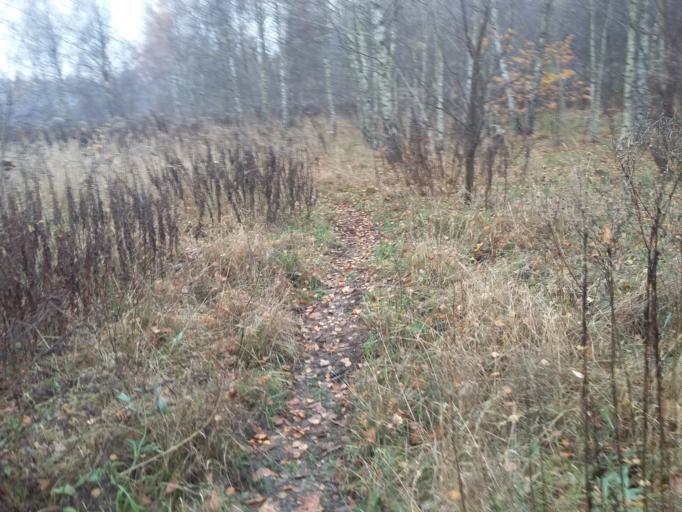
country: PL
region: Lodz Voivodeship
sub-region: Powiat pabianicki
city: Ksawerow
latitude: 51.7297
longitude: 19.3964
